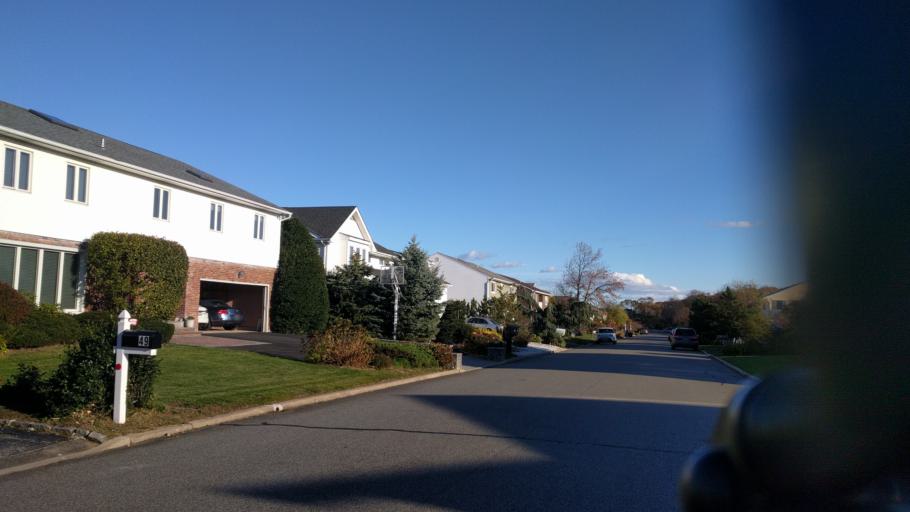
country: US
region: New York
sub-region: Nassau County
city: Bayville
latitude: 40.9149
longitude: -73.5662
